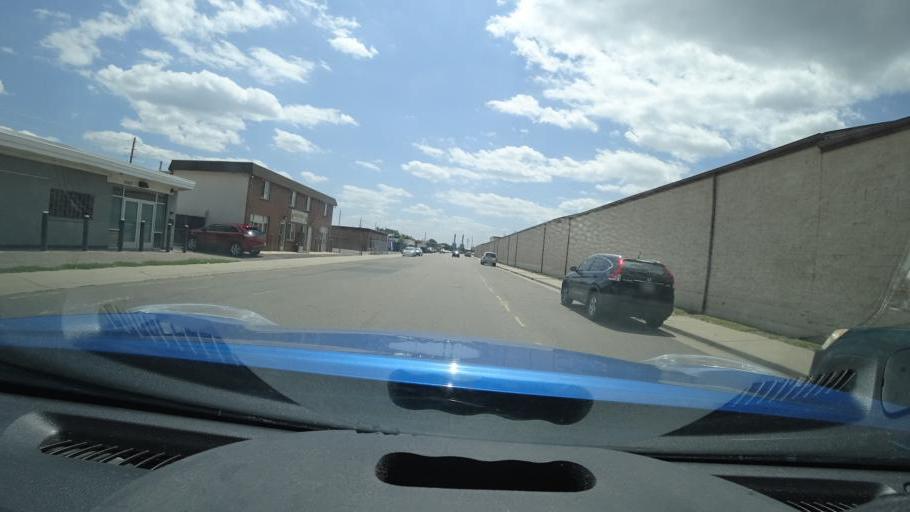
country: US
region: Colorado
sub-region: Arapahoe County
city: Englewood
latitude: 39.6774
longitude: -105.0018
